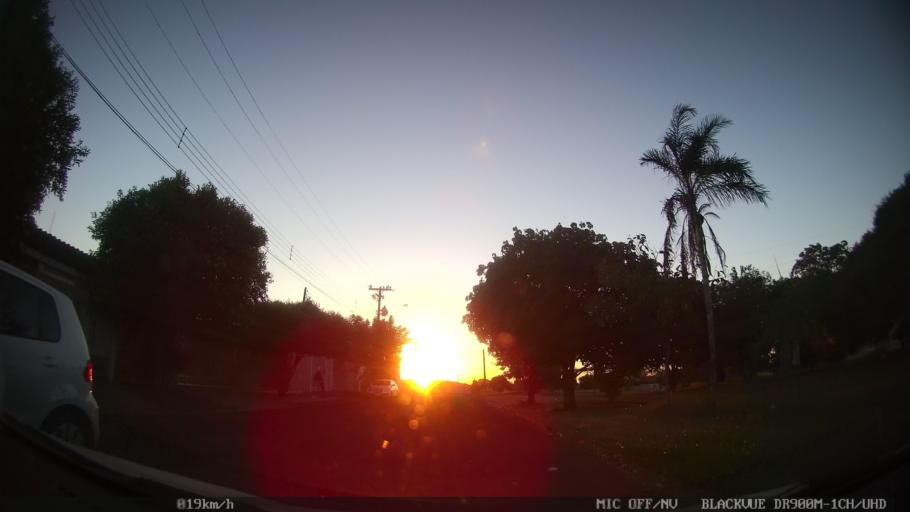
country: BR
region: Sao Paulo
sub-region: Sao Jose Do Rio Preto
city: Sao Jose do Rio Preto
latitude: -20.7962
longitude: -49.3459
